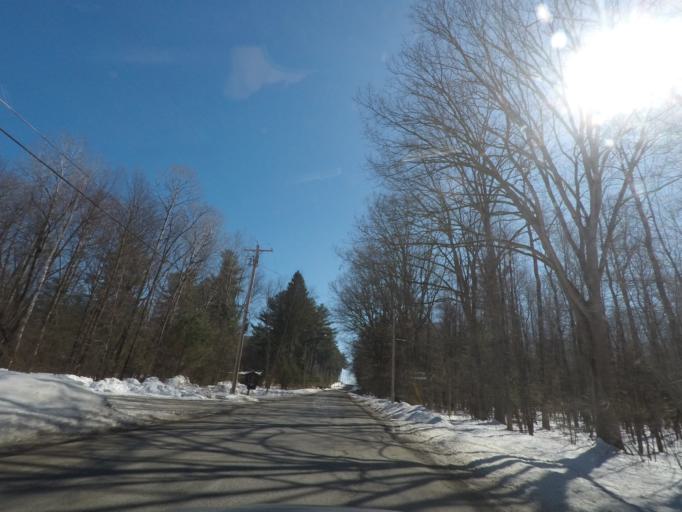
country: US
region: New York
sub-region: Saratoga County
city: Stillwater
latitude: 42.9215
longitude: -73.6217
